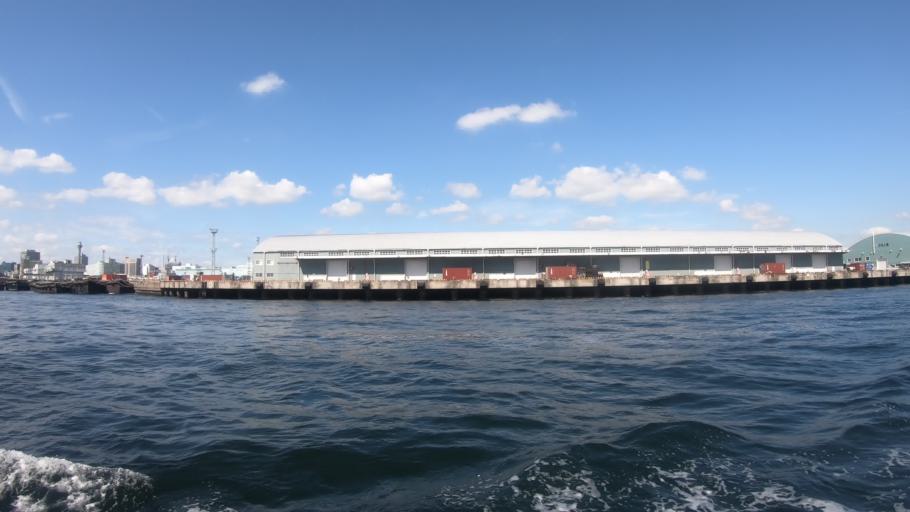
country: JP
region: Kanagawa
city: Yokohama
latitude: 35.4468
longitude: 139.6648
